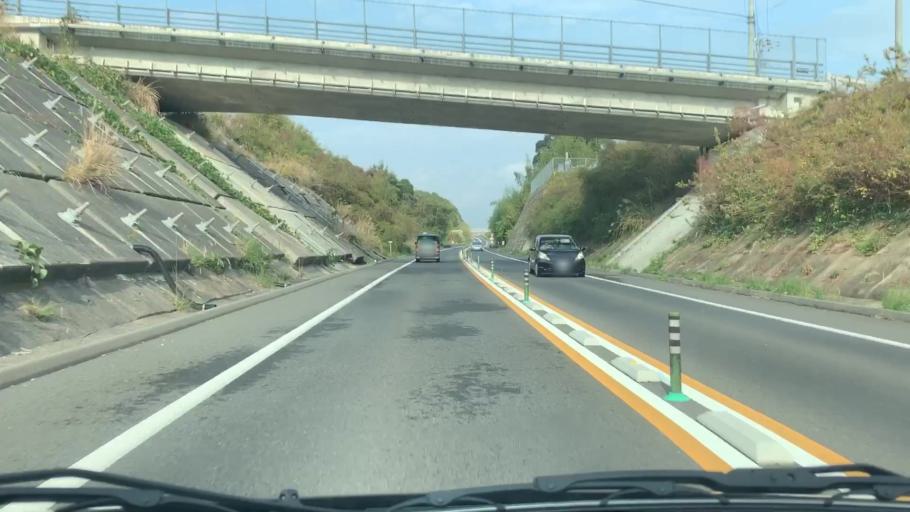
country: JP
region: Nagasaki
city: Sasebo
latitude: 33.0205
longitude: 129.7330
